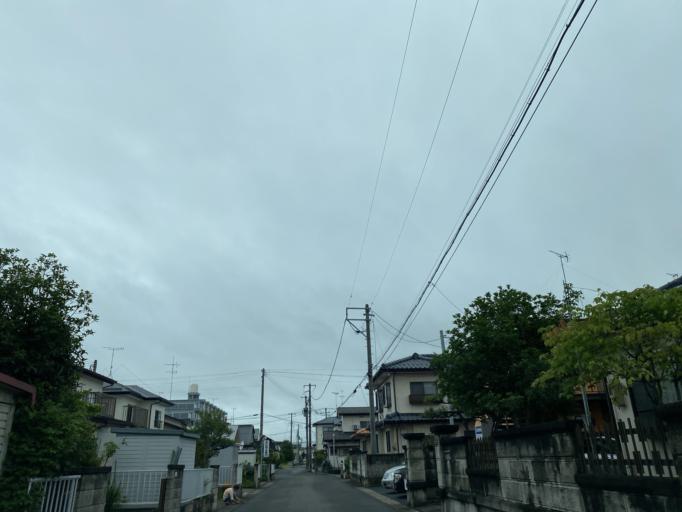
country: JP
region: Fukushima
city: Koriyama
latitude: 37.3925
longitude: 140.3246
